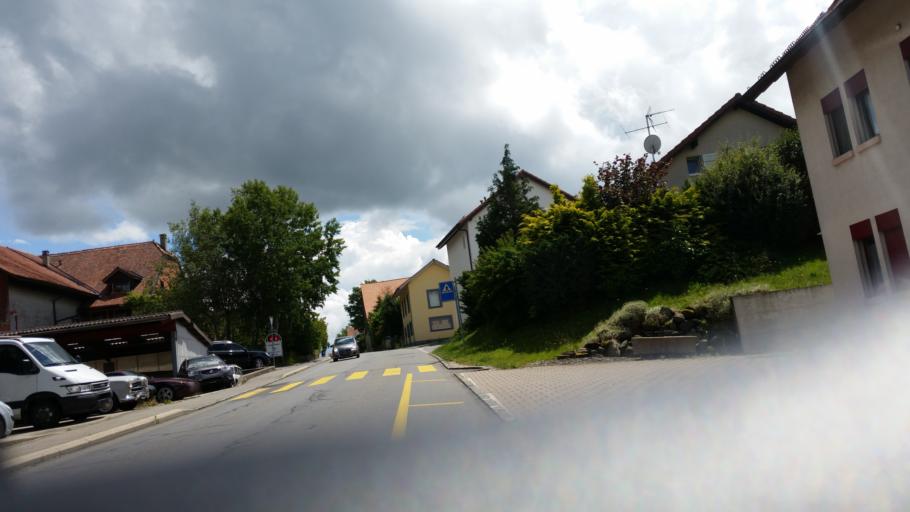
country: CH
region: Vaud
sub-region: Gros-de-Vaud District
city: Sottens
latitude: 46.7024
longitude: 6.7565
